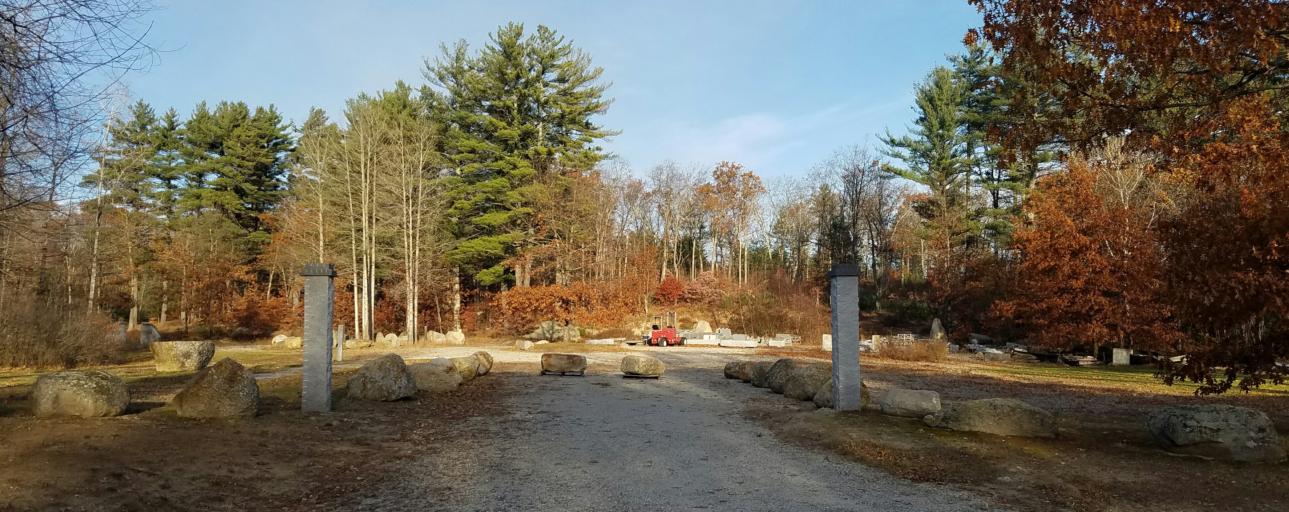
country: US
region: New Hampshire
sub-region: Merrimack County
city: Henniker
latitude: 43.1821
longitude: -71.7849
